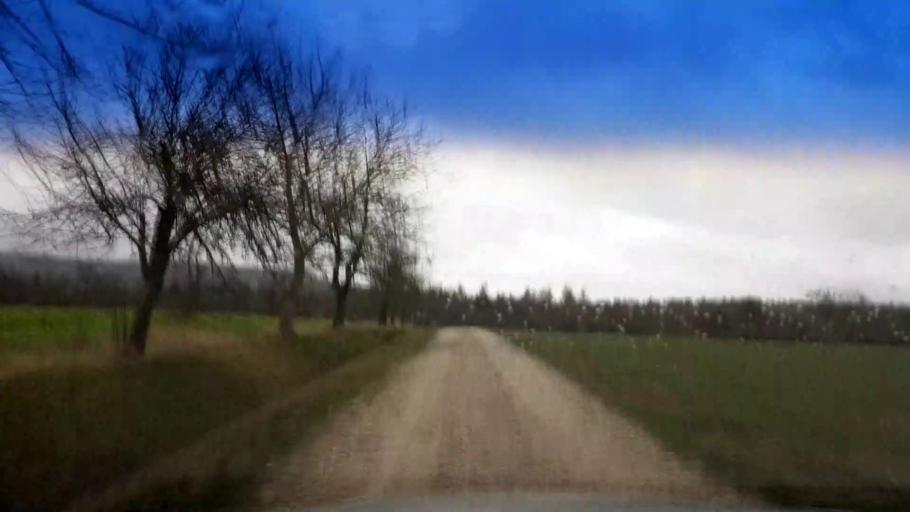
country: DE
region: Bavaria
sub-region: Upper Franconia
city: Litzendorf
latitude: 49.8673
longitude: 11.0317
